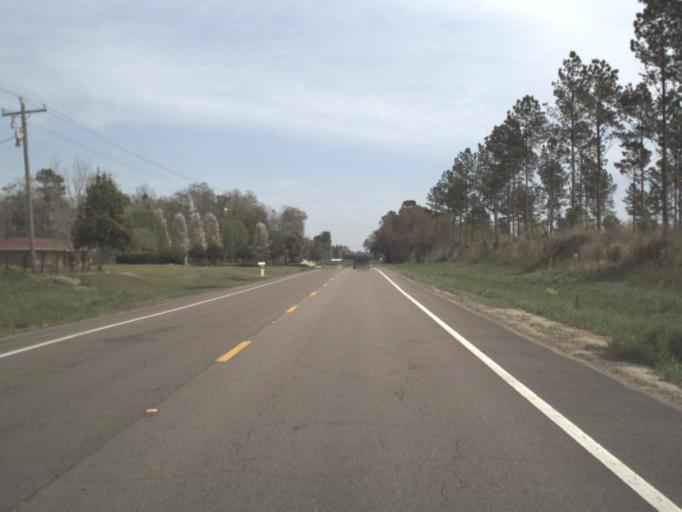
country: US
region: Alabama
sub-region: Geneva County
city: Hartford
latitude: 30.9551
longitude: -85.7210
